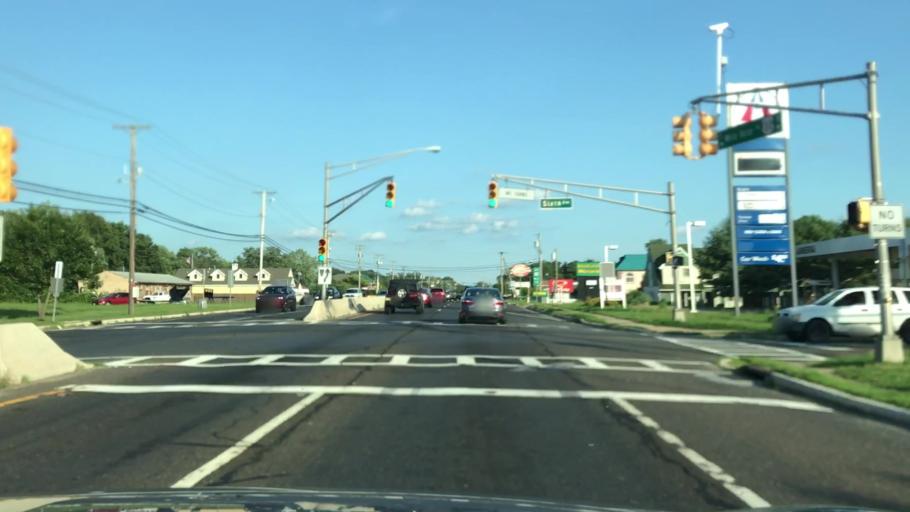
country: US
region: New Jersey
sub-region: Atlantic County
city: Absecon
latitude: 39.4444
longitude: -74.5261
